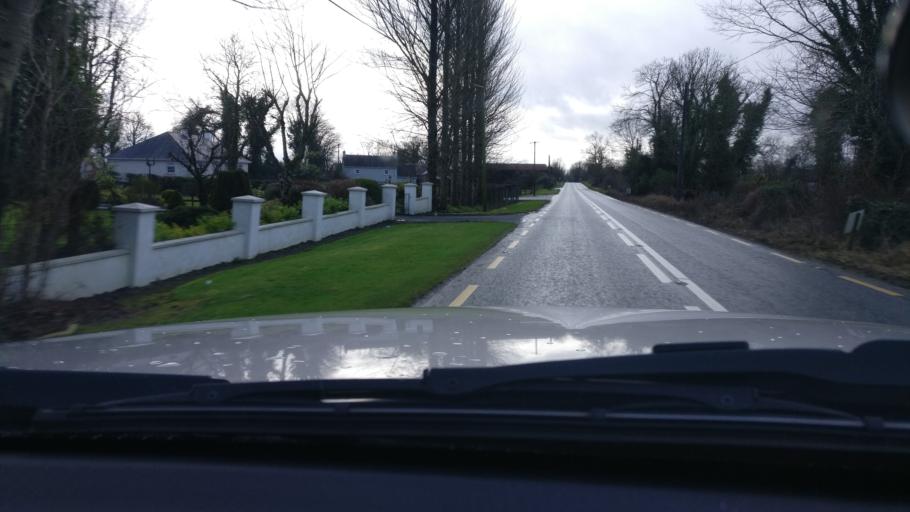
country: IE
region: Leinster
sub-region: An Iarmhi
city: Moate
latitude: 53.6178
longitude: -7.7028
